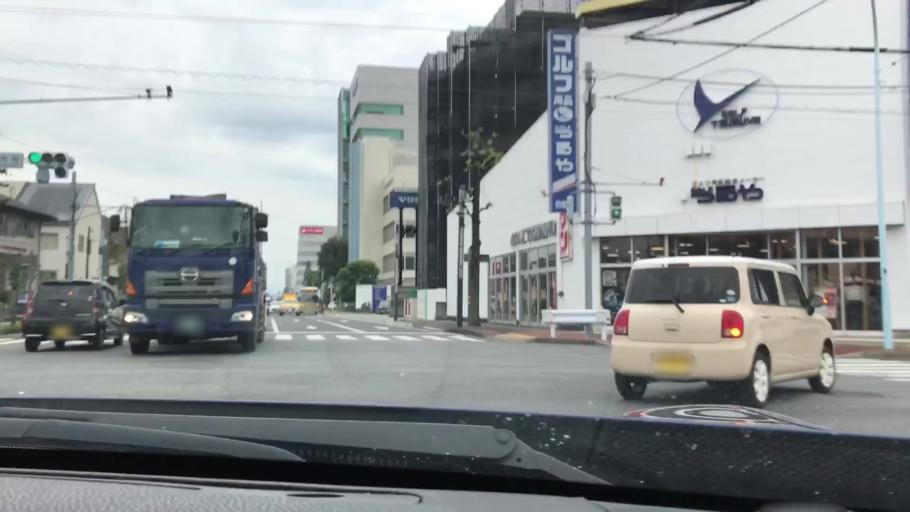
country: JP
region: Gunma
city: Maebashi-shi
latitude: 36.3743
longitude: 139.0442
